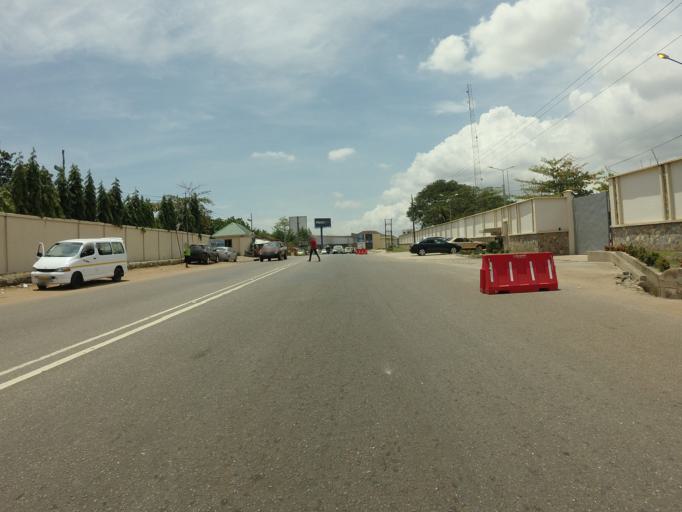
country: GH
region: Greater Accra
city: Medina Estates
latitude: 5.6272
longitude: -0.1519
